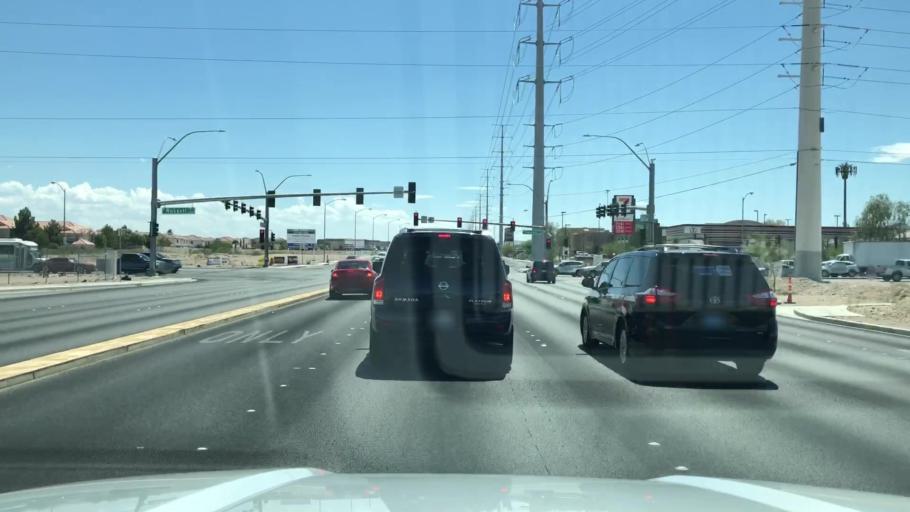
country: US
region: Nevada
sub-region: Clark County
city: Spring Valley
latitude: 36.0859
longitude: -115.2793
